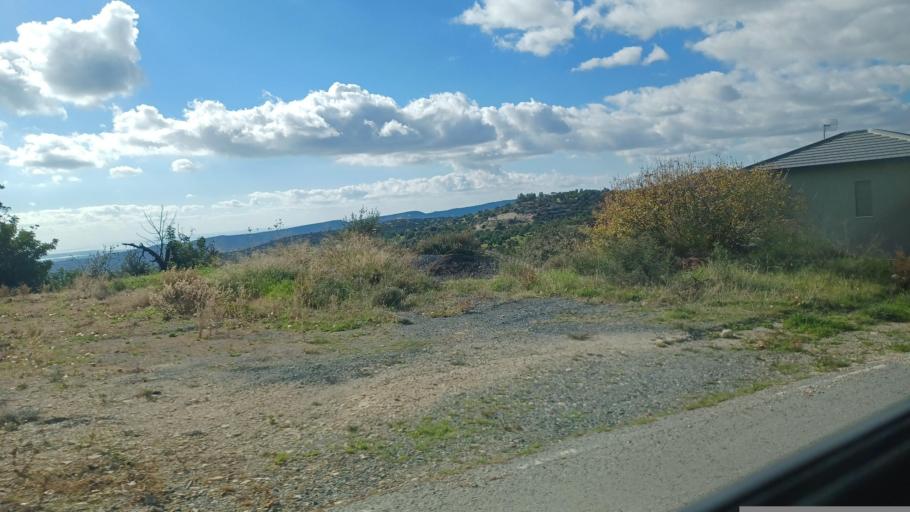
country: CY
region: Limassol
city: Pano Polemidia
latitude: 34.7918
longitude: 32.9873
